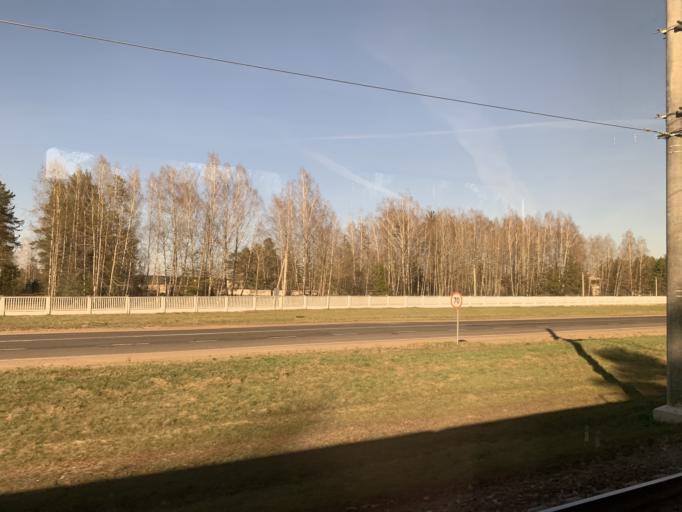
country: BY
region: Grodnenskaya
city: Smarhon'
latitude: 54.4398
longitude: 26.5058
